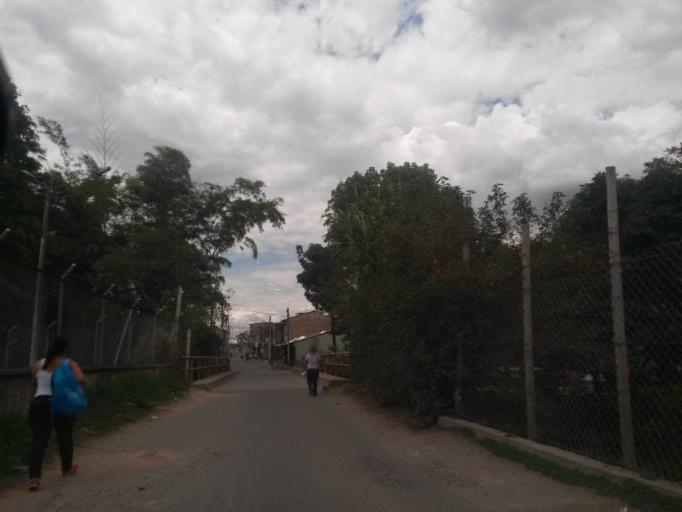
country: CO
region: Cauca
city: Popayan
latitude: 2.4473
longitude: -76.6258
